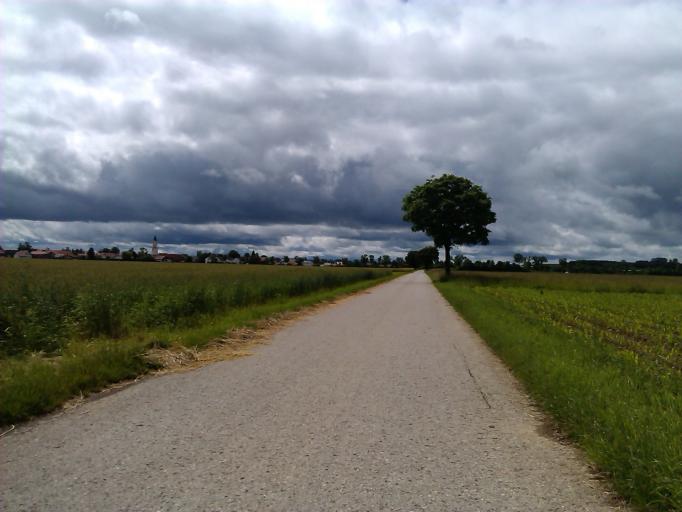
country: DE
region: Bavaria
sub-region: Swabia
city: Bad Worishofen
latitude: 47.9784
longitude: 10.6140
